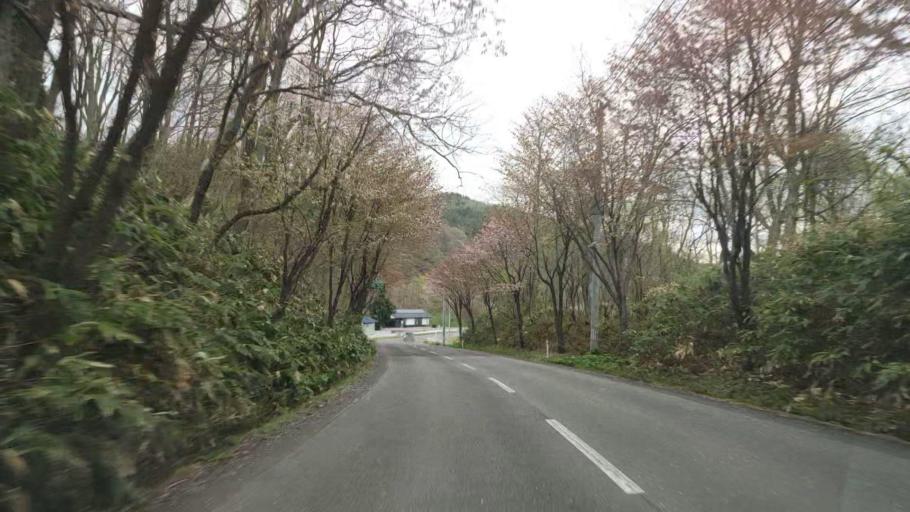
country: JP
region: Akita
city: Hanawa
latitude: 40.3606
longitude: 140.7852
